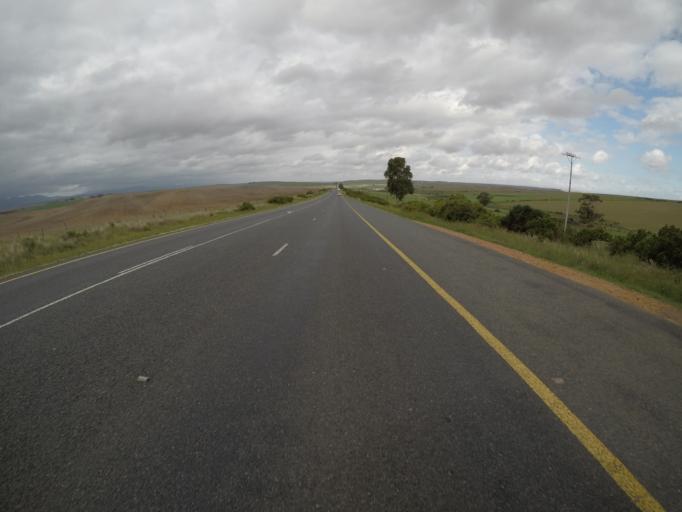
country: ZA
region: Western Cape
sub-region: Overberg District Municipality
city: Swellendam
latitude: -34.1146
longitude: 20.8283
